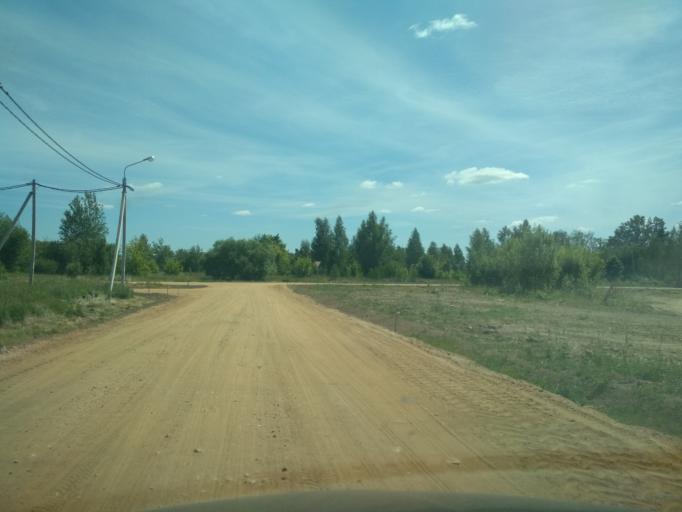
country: BY
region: Minsk
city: Mar''ina Horka
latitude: 53.5101
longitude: 28.1636
